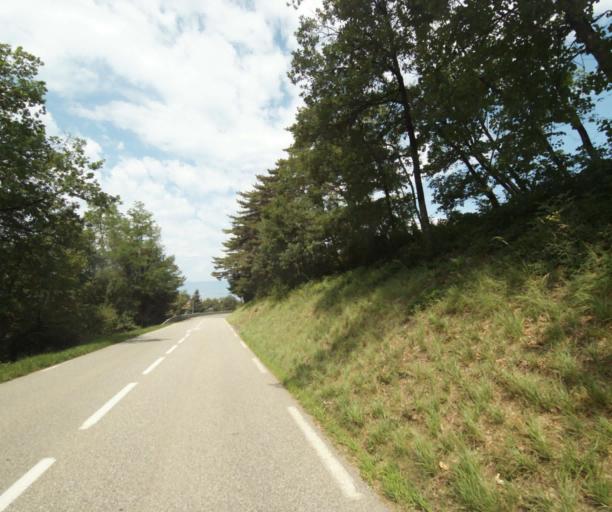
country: FR
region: Rhone-Alpes
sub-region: Departement de la Haute-Savoie
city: Thonon-les-Bains
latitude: 46.3603
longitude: 6.4930
